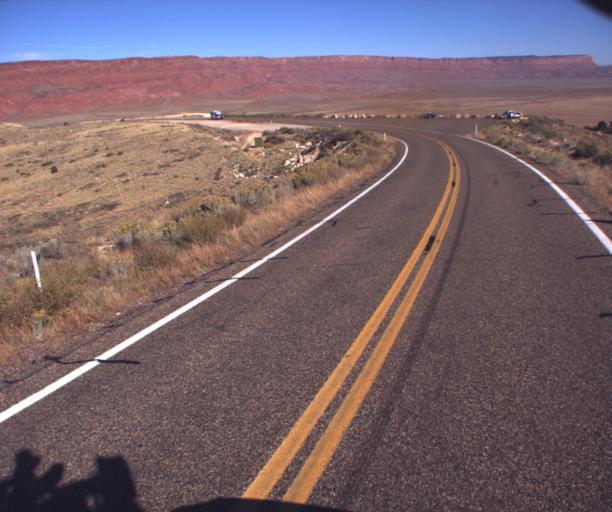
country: US
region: Arizona
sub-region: Coconino County
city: Fredonia
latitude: 36.7227
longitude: -112.0620
